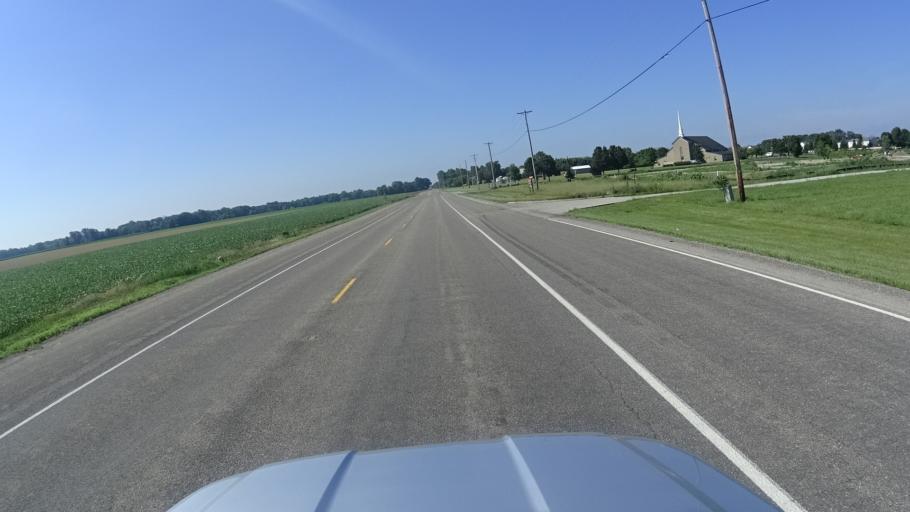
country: US
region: Indiana
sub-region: Madison County
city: Ingalls
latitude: 39.9872
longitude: -85.8432
